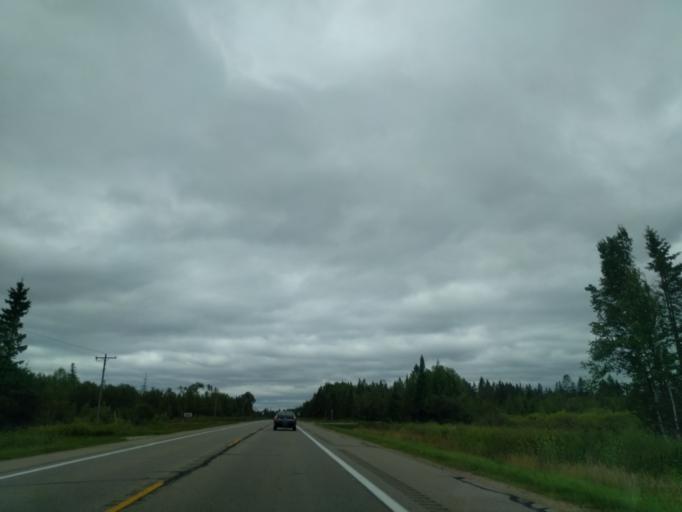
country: US
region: Michigan
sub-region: Delta County
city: Escanaba
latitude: 45.6371
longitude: -87.1993
